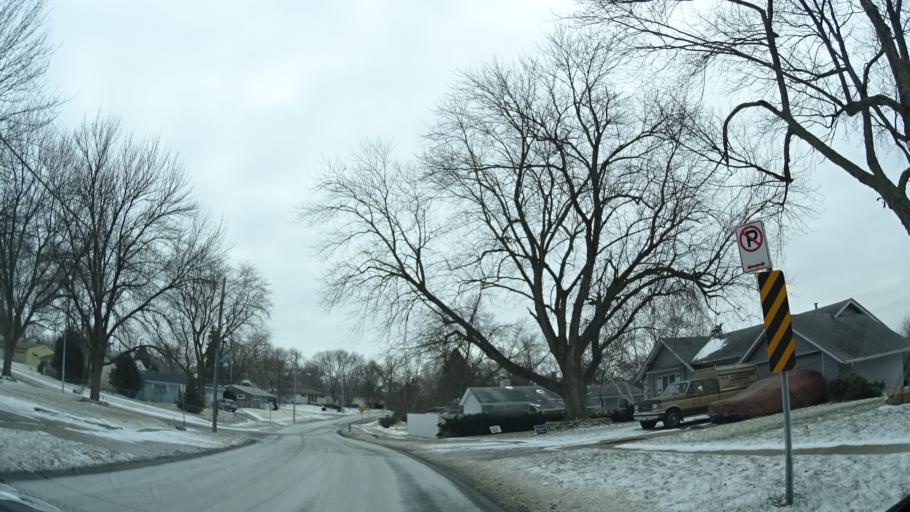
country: US
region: Nebraska
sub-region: Douglas County
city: Omaha
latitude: 41.2303
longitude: -95.9854
